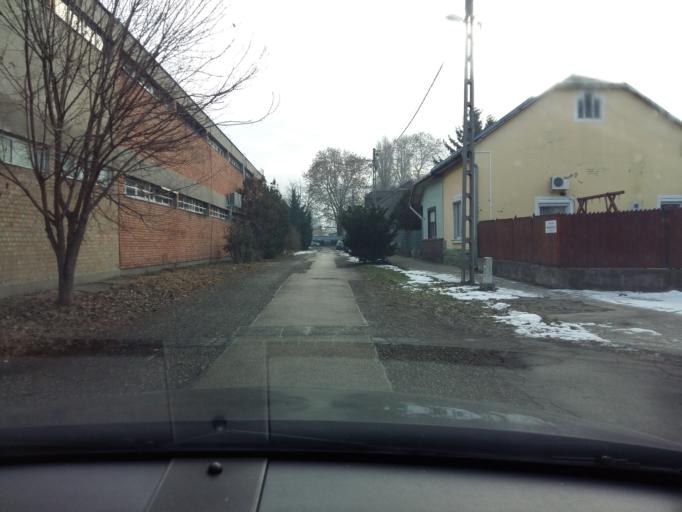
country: HU
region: Budapest
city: Budapest IV. keruelet
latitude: 47.5489
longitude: 19.0998
